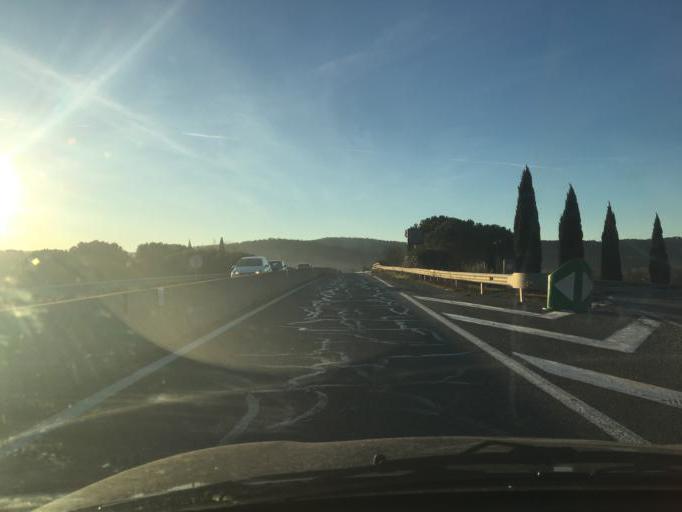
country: FR
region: Provence-Alpes-Cote d'Azur
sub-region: Departement du Var
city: Les Arcs
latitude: 43.4510
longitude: 6.4920
